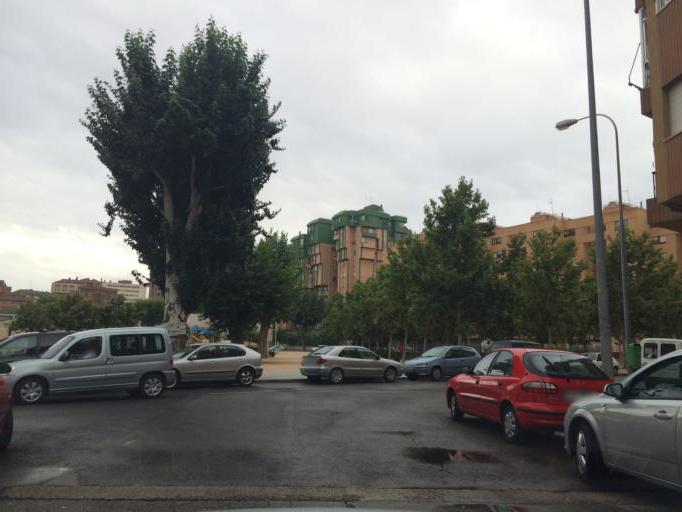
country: ES
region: Castille-La Mancha
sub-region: Provincia de Albacete
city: Albacete
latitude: 39.0011
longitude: -1.8533
